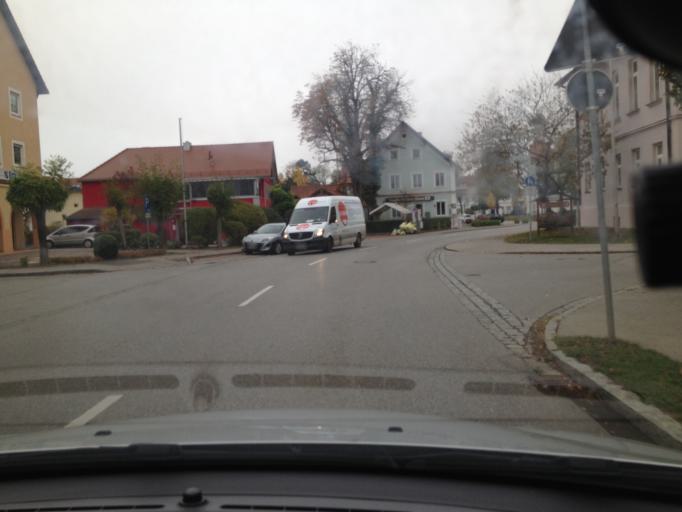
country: DE
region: Bavaria
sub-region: Swabia
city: Klosterlechfeld
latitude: 48.1579
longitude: 10.8323
